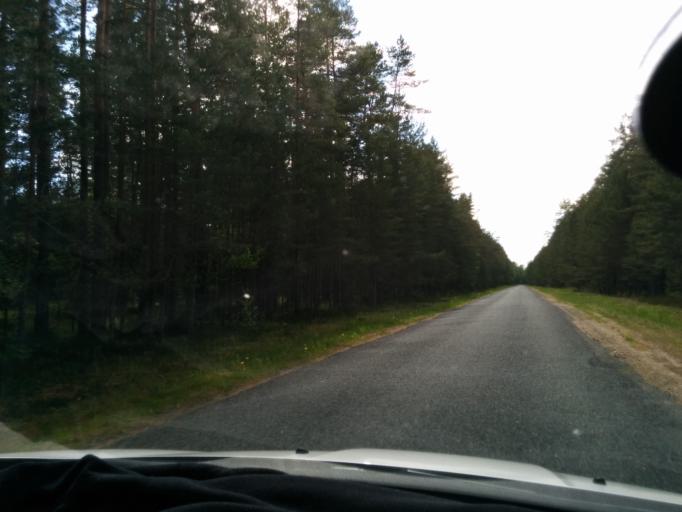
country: EE
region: Harju
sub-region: Loksa linn
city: Loksa
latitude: 59.5668
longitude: 25.6987
